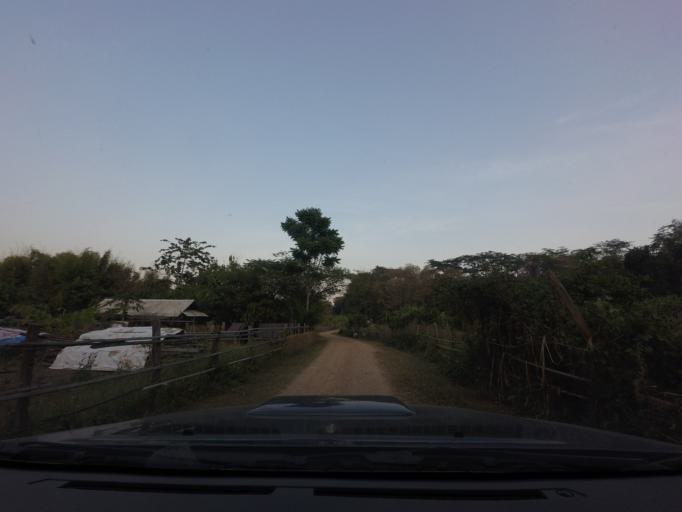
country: TH
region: Chiang Mai
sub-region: Amphoe Chiang Dao
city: Chiang Dao
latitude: 19.3627
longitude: 98.9270
